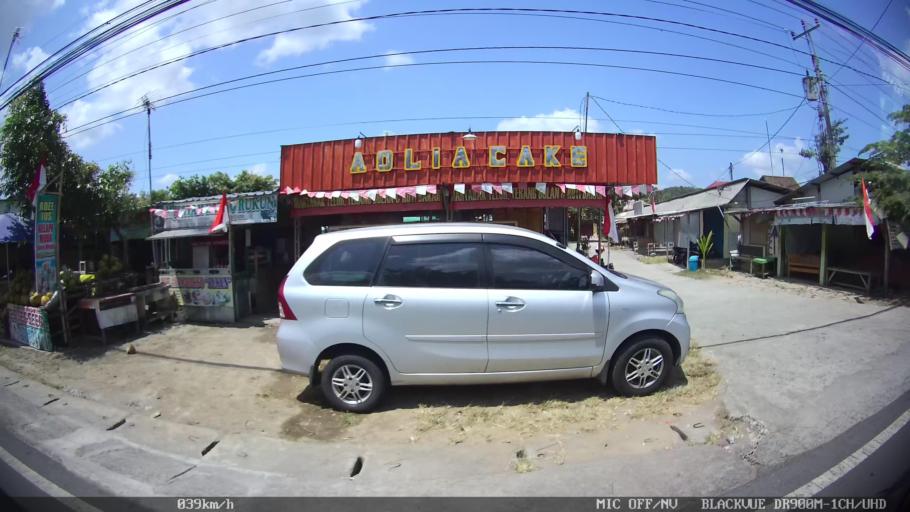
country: ID
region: Daerah Istimewa Yogyakarta
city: Sewon
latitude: -7.9100
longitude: 110.3829
